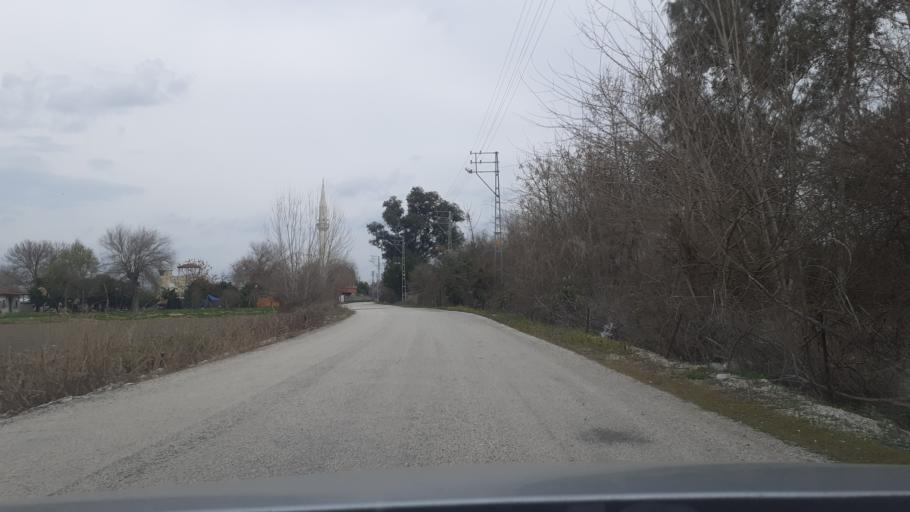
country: TR
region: Osmaniye
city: Sumbas
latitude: 37.3732
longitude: 35.9705
